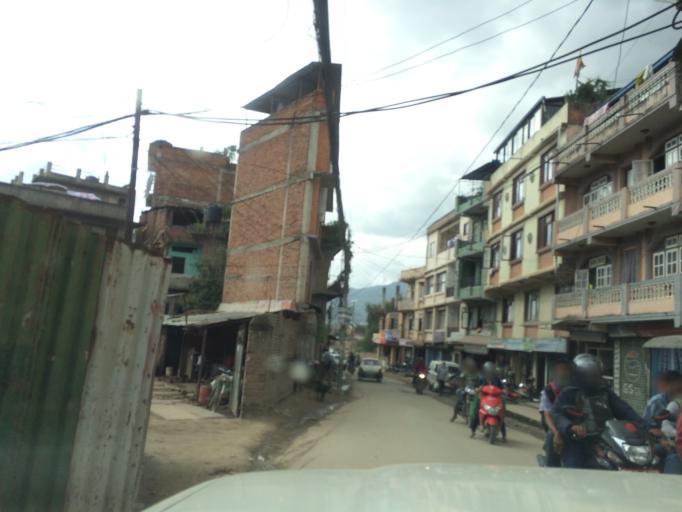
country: NP
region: Central Region
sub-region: Bagmati Zone
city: Patan
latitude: 27.6914
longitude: 85.3052
